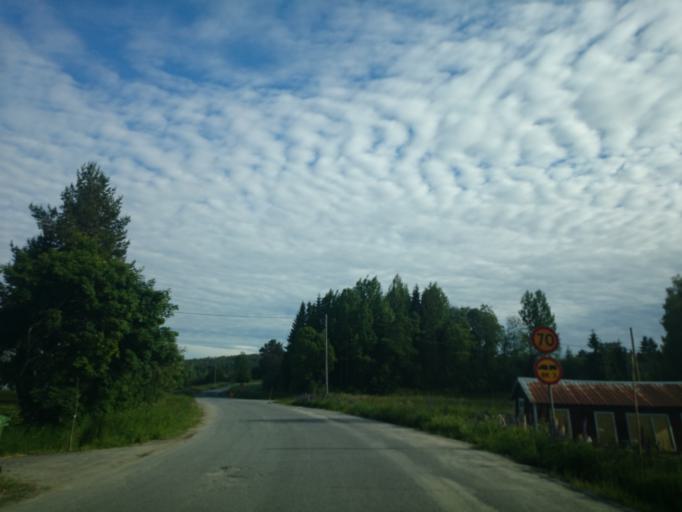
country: SE
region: Vaesternorrland
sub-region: Haernoesands Kommun
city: Haernoesand
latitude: 62.6366
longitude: 17.8468
